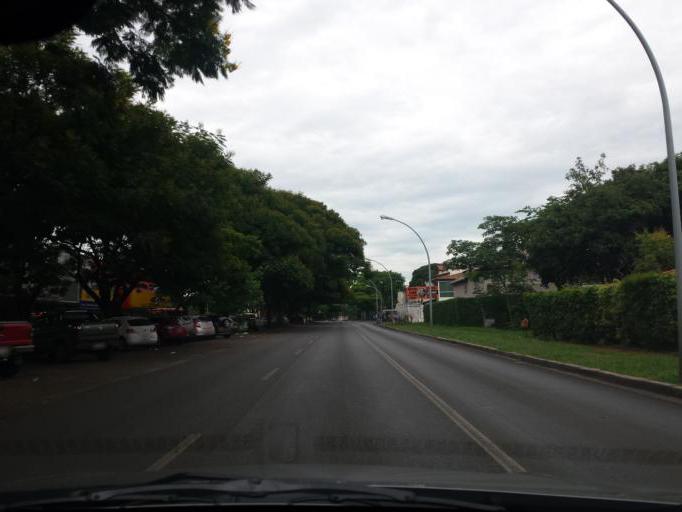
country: BR
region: Federal District
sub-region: Brasilia
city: Brasilia
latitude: -15.8225
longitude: -47.9204
